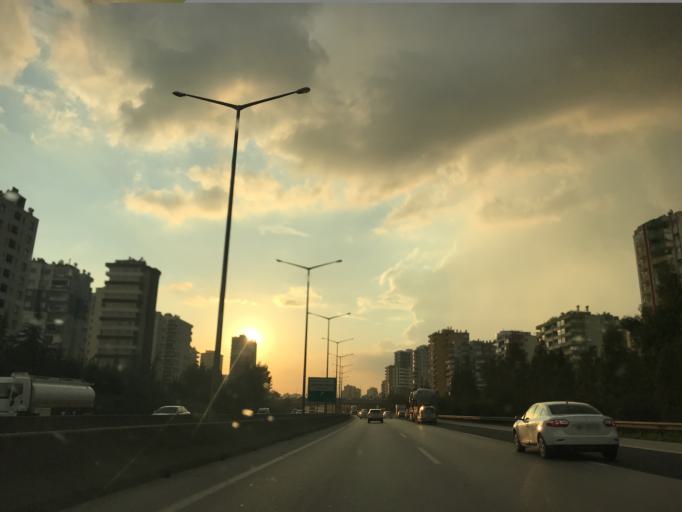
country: TR
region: Adana
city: Adana
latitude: 37.0329
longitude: 35.2945
